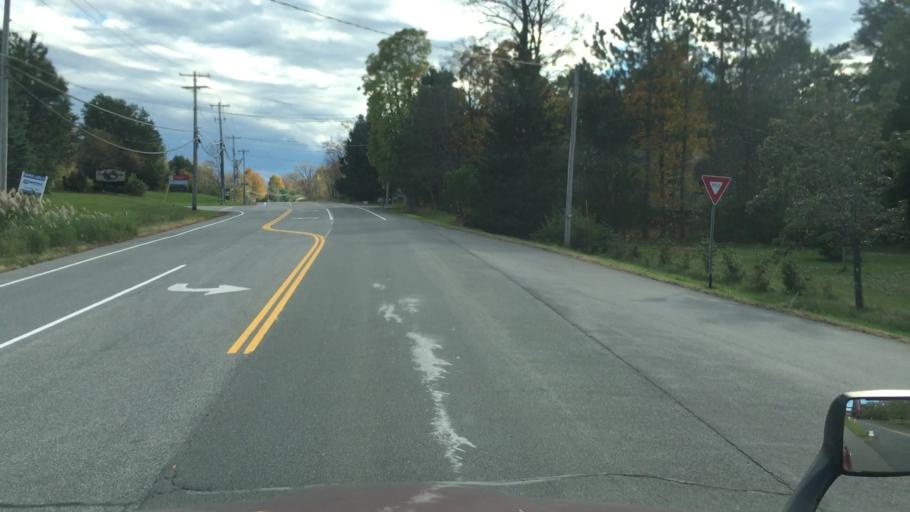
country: US
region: New York
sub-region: Saratoga County
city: Ballston Spa
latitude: 42.9678
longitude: -73.8636
